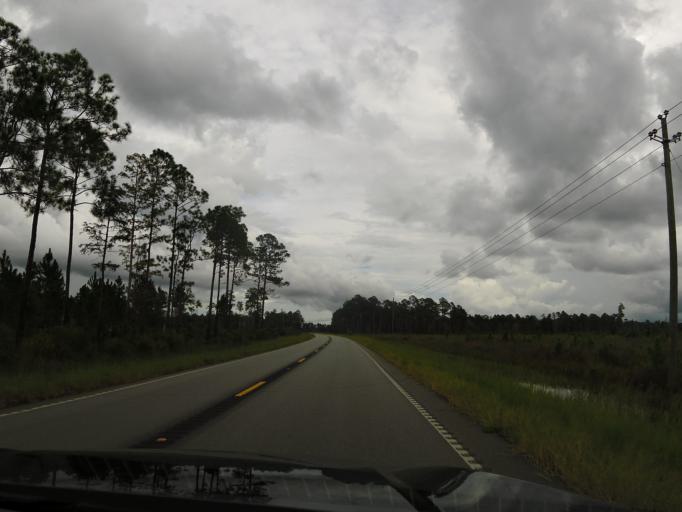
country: US
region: Florida
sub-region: Baker County
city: Macclenny
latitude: 30.5245
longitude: -82.1664
